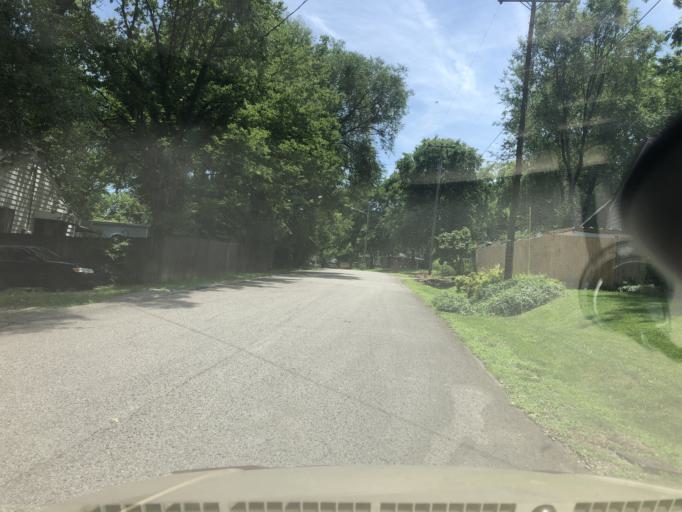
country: US
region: Tennessee
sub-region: Davidson County
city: Lakewood
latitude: 36.2573
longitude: -86.6996
